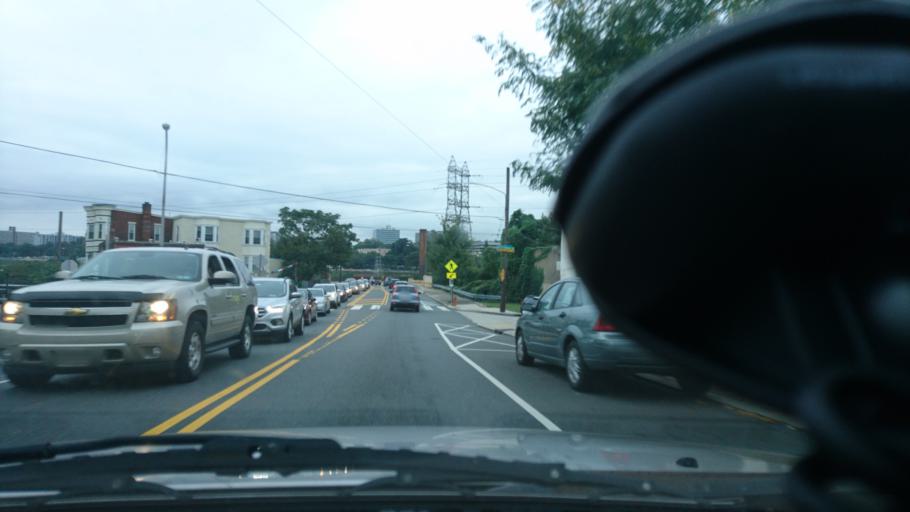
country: US
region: Pennsylvania
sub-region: Montgomery County
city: Bala-Cynwyd
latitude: 40.0181
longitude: -75.2114
